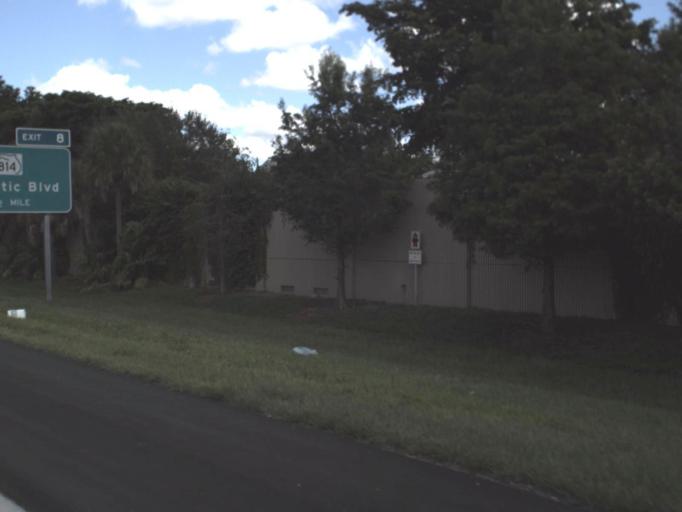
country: US
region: Florida
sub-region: Broward County
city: Tamarac
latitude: 26.2205
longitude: -80.2963
